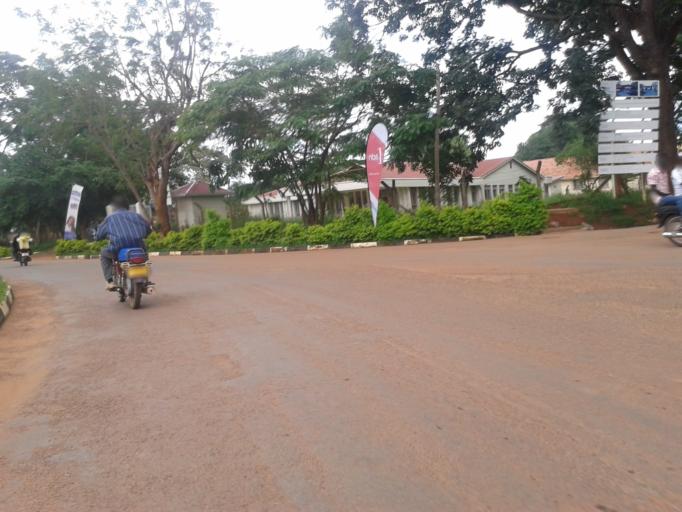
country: UG
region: Northern Region
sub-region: Gulu District
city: Gulu
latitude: 2.7791
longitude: 32.2967
